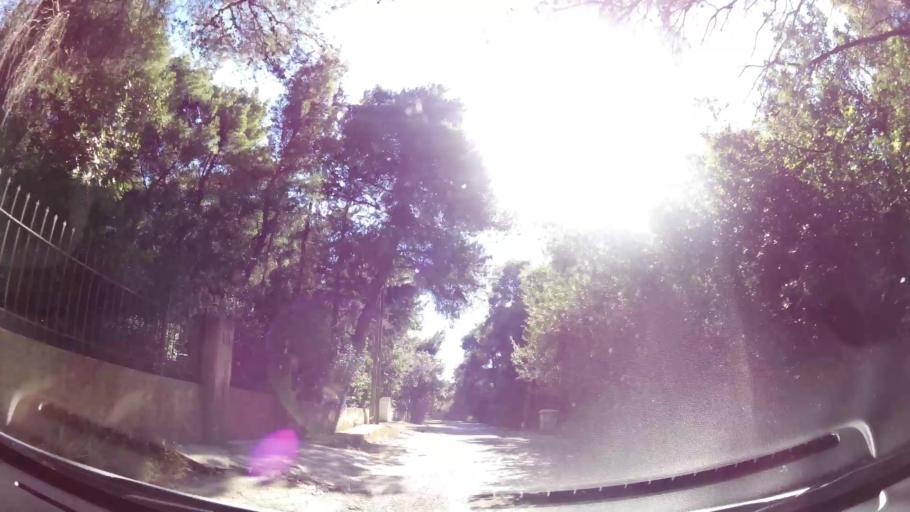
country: GR
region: Attica
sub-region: Nomarchia Athinas
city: Ekali
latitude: 38.1094
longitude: 23.8259
